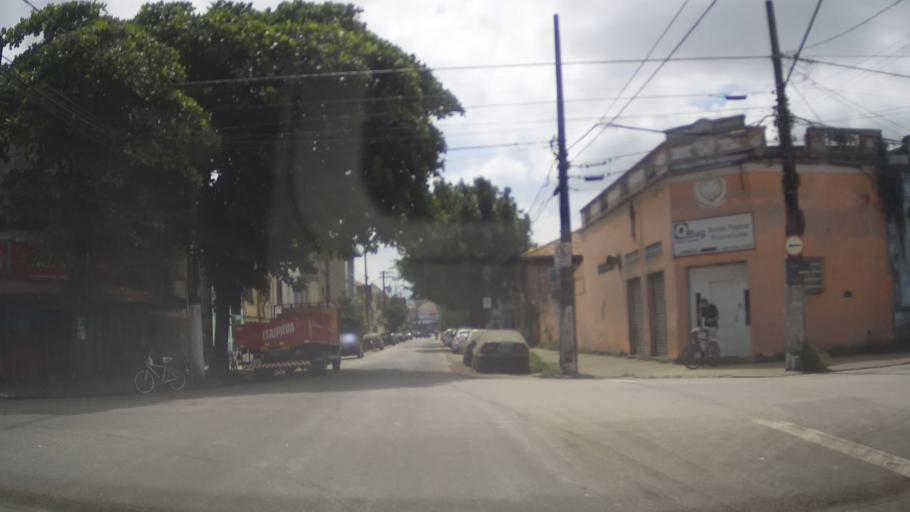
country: BR
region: Sao Paulo
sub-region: Santos
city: Santos
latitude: -23.9544
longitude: -46.3163
